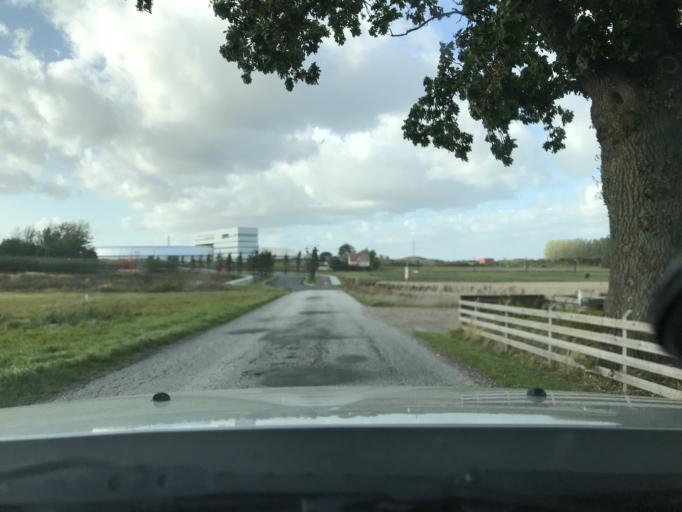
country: SE
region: Skane
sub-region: Lunds Kommun
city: Lund
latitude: 55.7237
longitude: 13.2389
